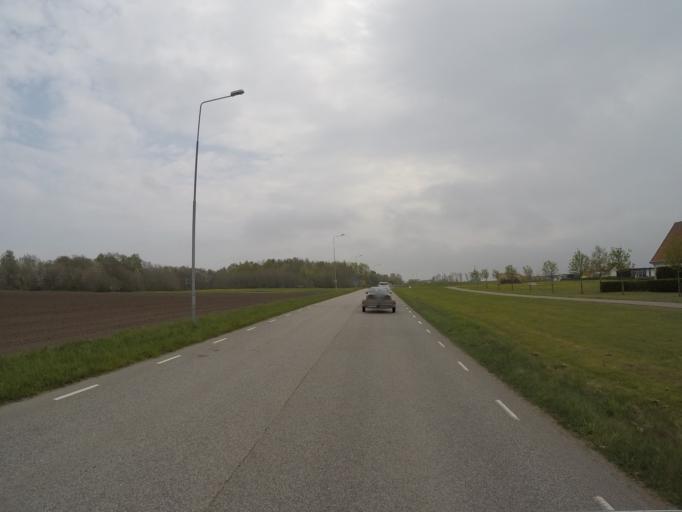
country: SE
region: Halland
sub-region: Laholms Kommun
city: Laholm
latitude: 56.5007
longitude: 13.0640
